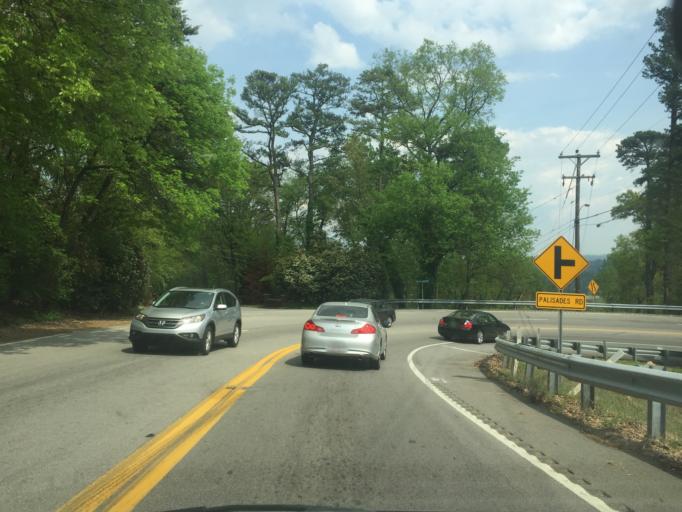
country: US
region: Tennessee
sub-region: Hamilton County
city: Signal Mountain
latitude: 35.1061
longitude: -85.3471
